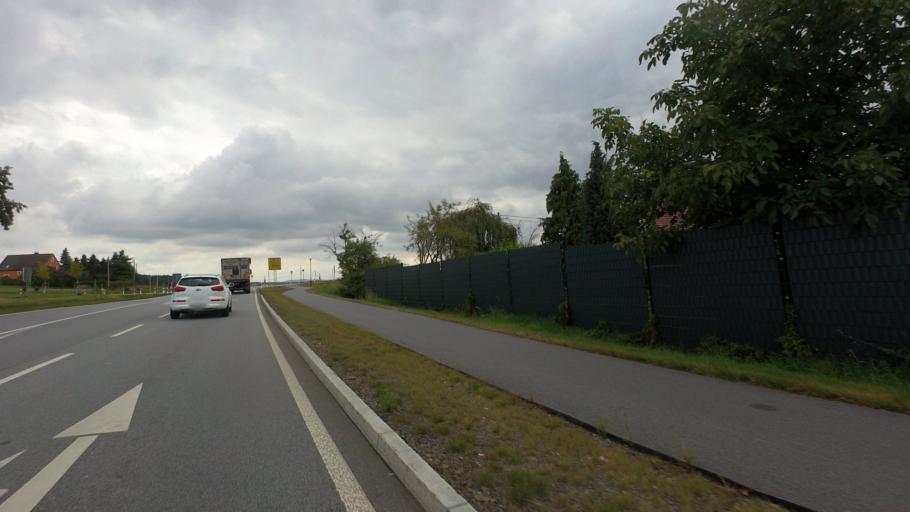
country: DE
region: Saxony
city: Neschwitz
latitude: 51.2494
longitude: 14.3555
